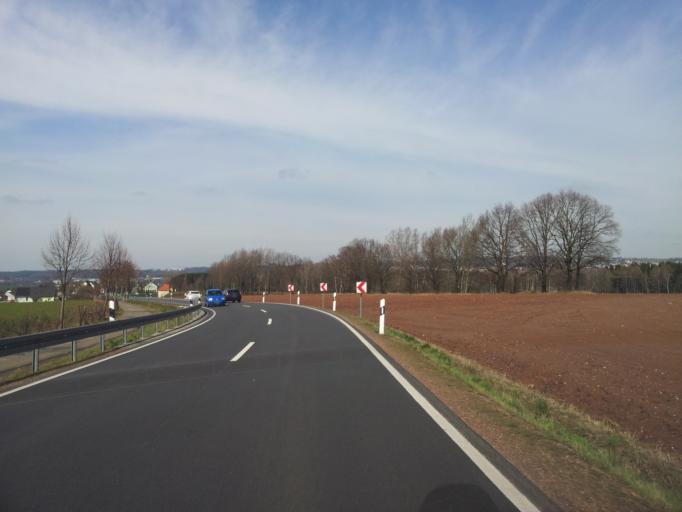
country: DE
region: Saxony
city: Gersdorf
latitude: 50.7637
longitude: 12.7163
